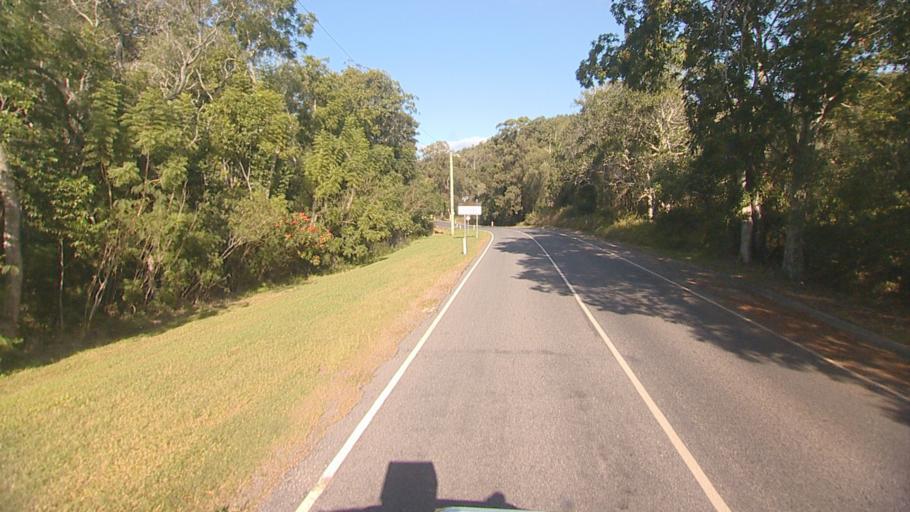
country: AU
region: Queensland
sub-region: Logan
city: Windaroo
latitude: -27.7389
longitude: 153.1783
